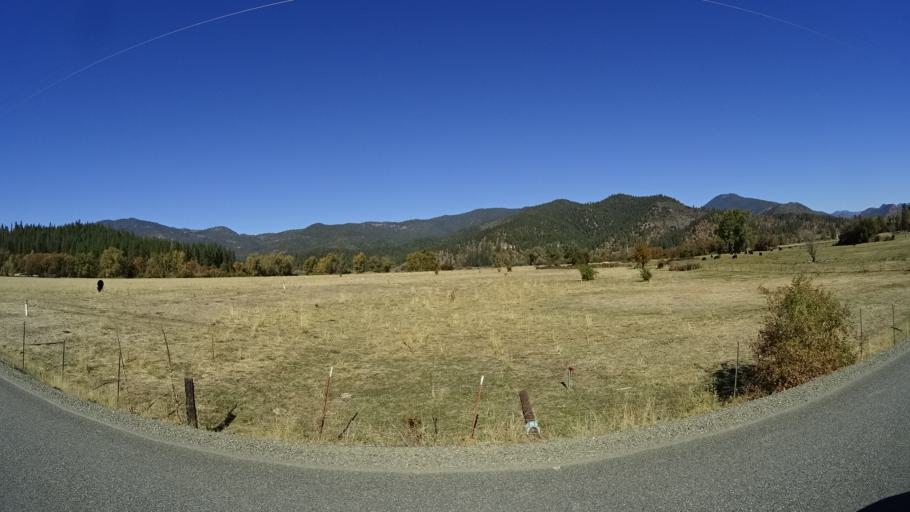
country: US
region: California
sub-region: Siskiyou County
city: Yreka
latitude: 41.6239
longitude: -122.9714
